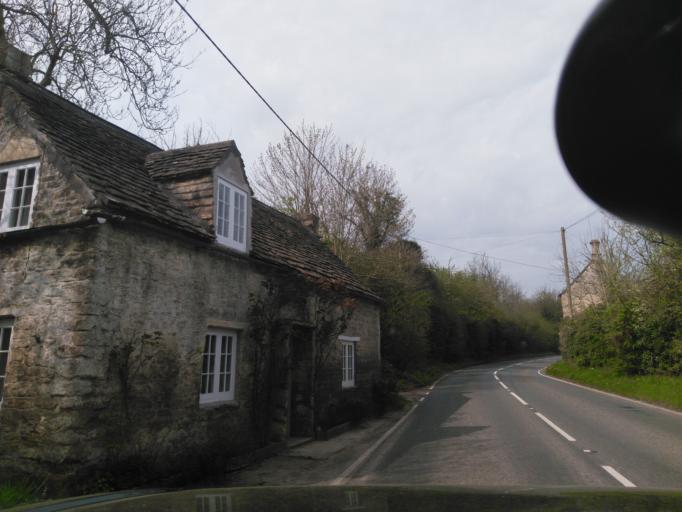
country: GB
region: England
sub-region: Wiltshire
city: Westwood
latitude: 51.3164
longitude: -2.2878
